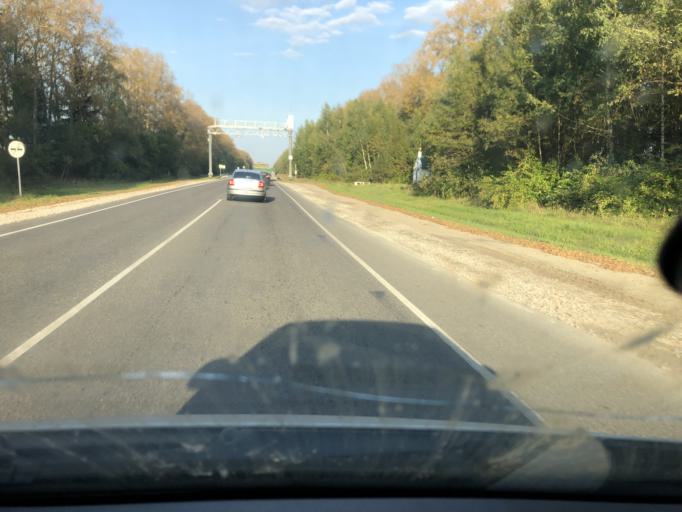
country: RU
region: Kaluga
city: Peremyshl'
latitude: 54.2491
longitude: 36.1031
